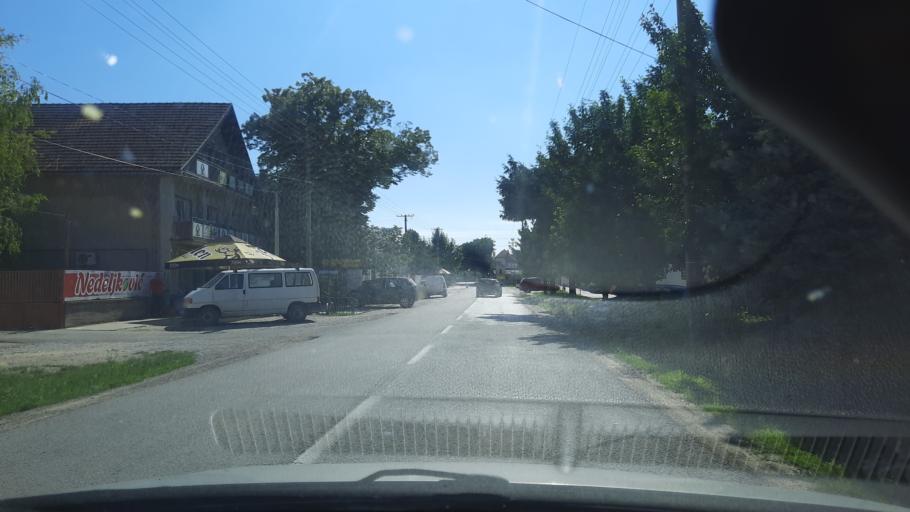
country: RS
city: Cortanovci
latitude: 45.1017
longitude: 19.9937
